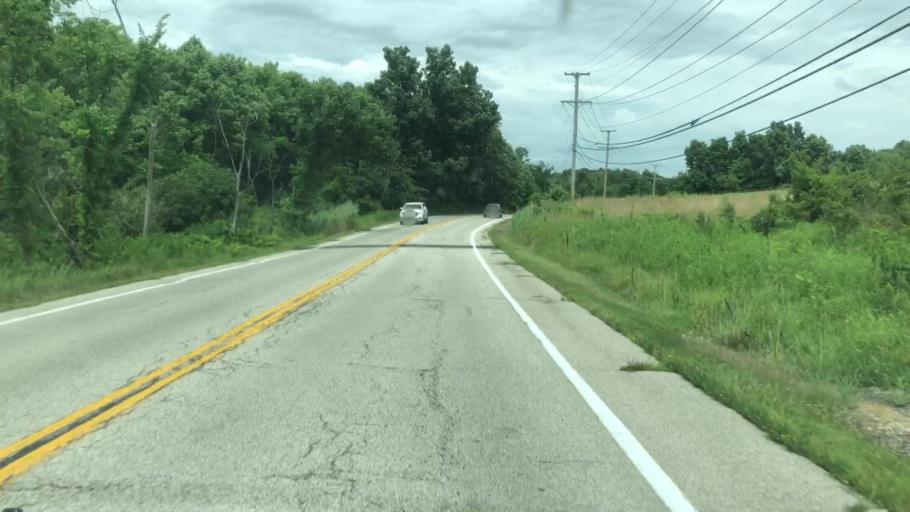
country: US
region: Ohio
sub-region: Summit County
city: Fairlawn
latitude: 41.1741
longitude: -81.5611
